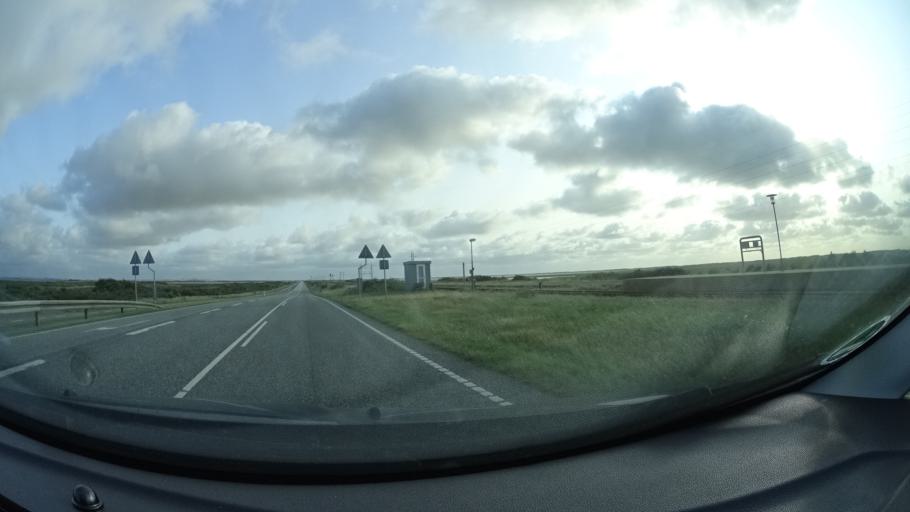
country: DK
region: Central Jutland
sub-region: Lemvig Kommune
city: Harboore
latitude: 56.6569
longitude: 8.1951
